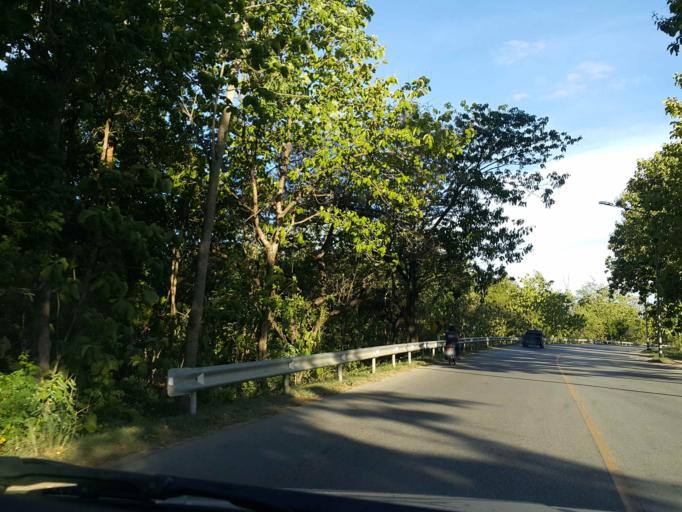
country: TH
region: Chiang Mai
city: Chom Thong
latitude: 18.4428
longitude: 98.6780
